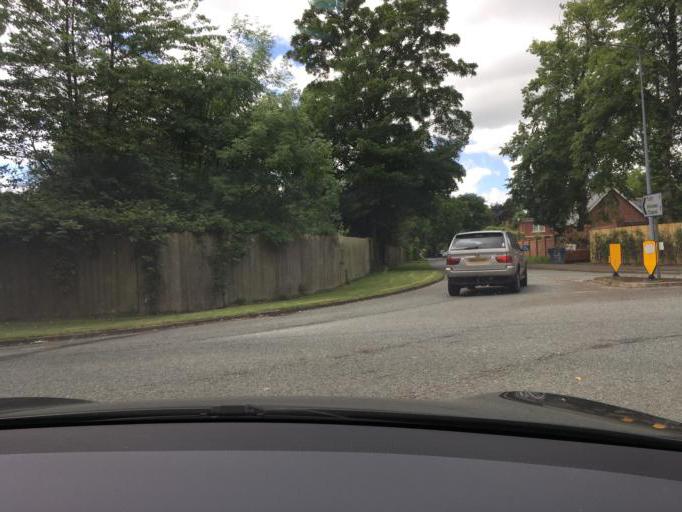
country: GB
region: England
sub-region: Cheshire East
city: Knutsford
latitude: 53.2942
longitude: -2.3549
